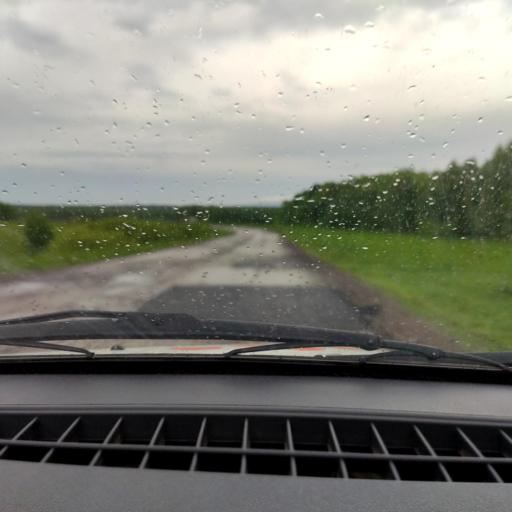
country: RU
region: Bashkortostan
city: Kudeyevskiy
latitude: 54.8507
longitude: 56.7993
